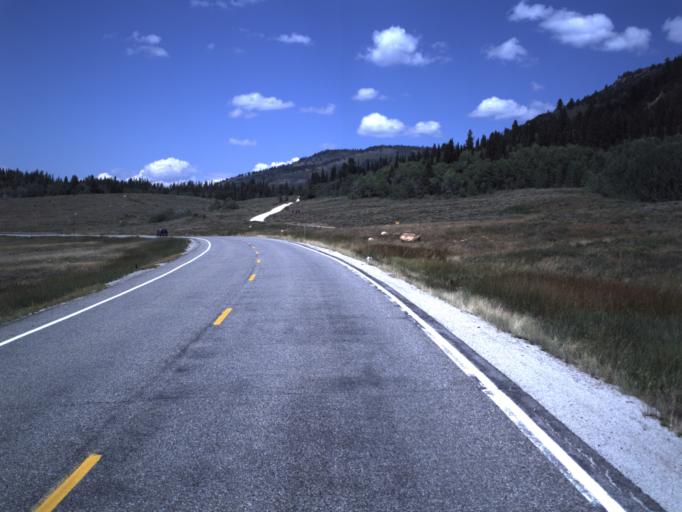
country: US
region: Idaho
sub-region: Bear Lake County
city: Paris
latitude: 41.9492
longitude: -111.4823
